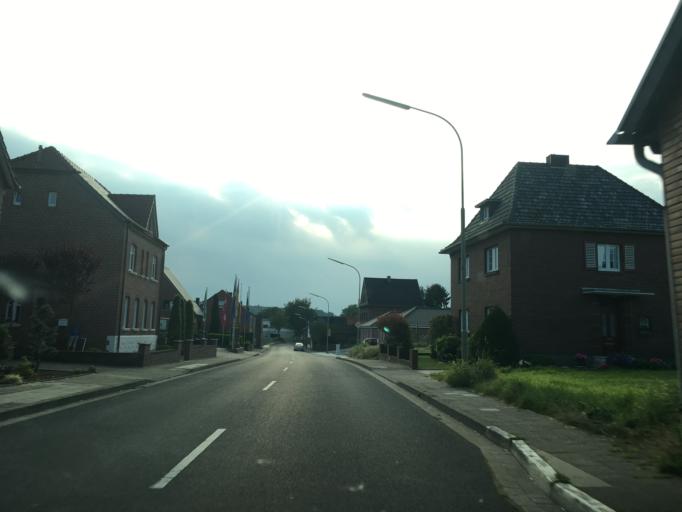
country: DE
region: North Rhine-Westphalia
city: Huckelhoven
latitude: 51.0772
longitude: 6.2210
